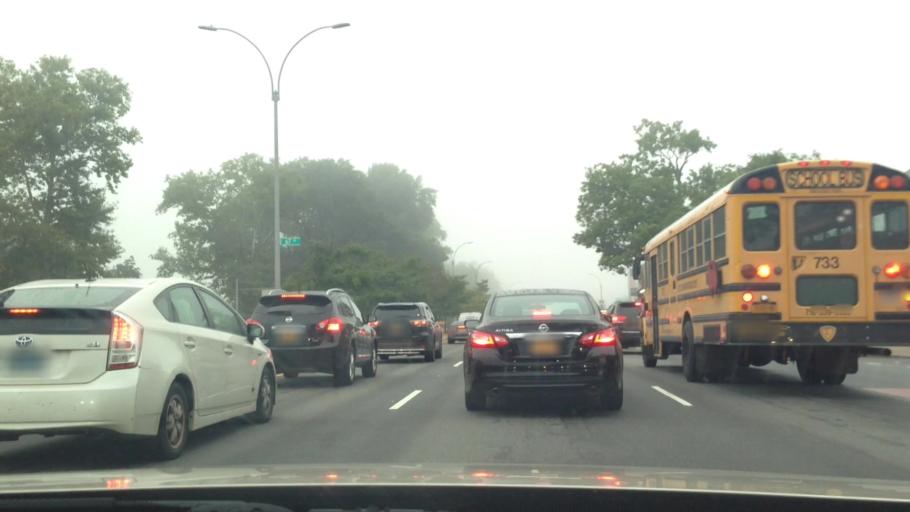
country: US
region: New York
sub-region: Queens County
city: Borough of Queens
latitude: 40.7170
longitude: -73.8622
